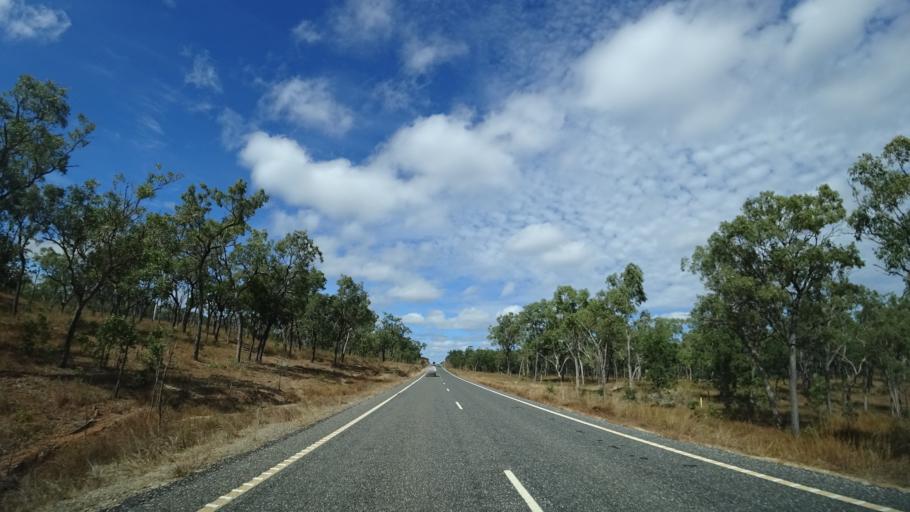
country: AU
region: Queensland
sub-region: Cairns
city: Port Douglas
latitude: -16.3123
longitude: 144.7178
